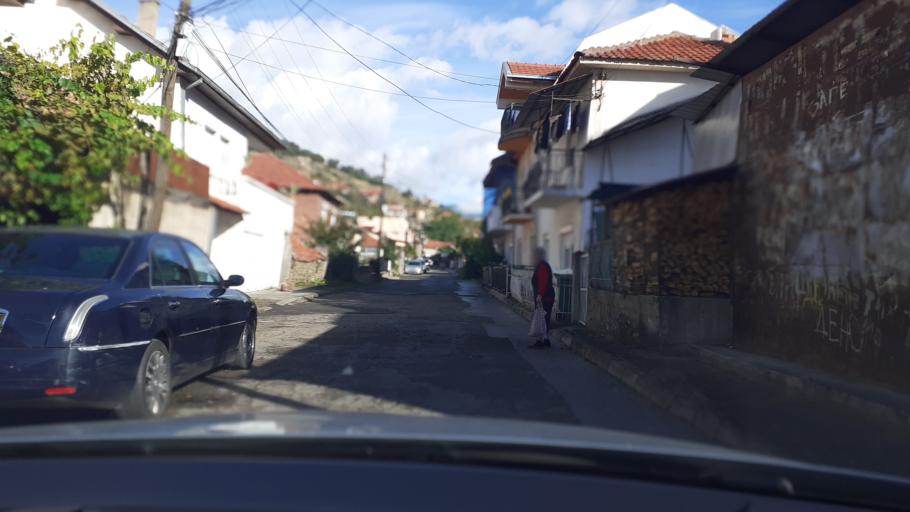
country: MK
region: Kocani
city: Kochani
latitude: 41.9263
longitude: 22.4111
